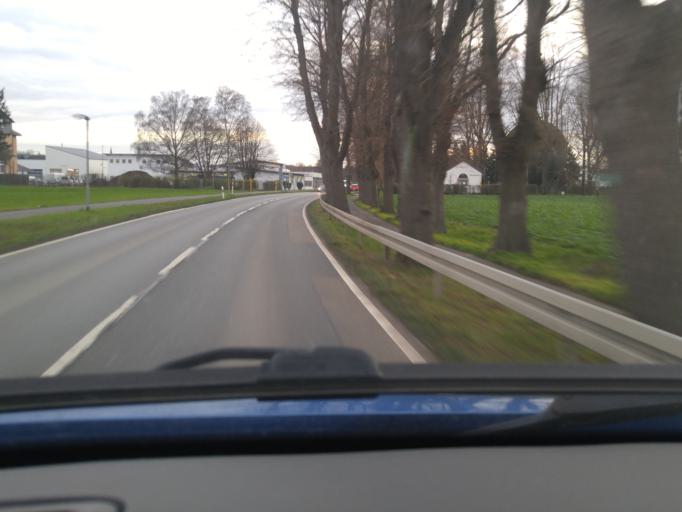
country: DE
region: Hesse
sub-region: Regierungsbezirk Darmstadt
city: Bad Nauheim
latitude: 50.3512
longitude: 8.7432
